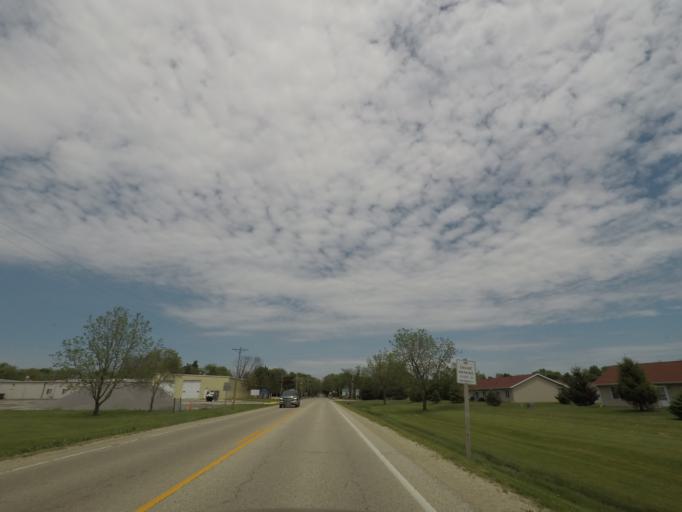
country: US
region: Wisconsin
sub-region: Rock County
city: Evansville
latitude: 42.7708
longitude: -89.2990
